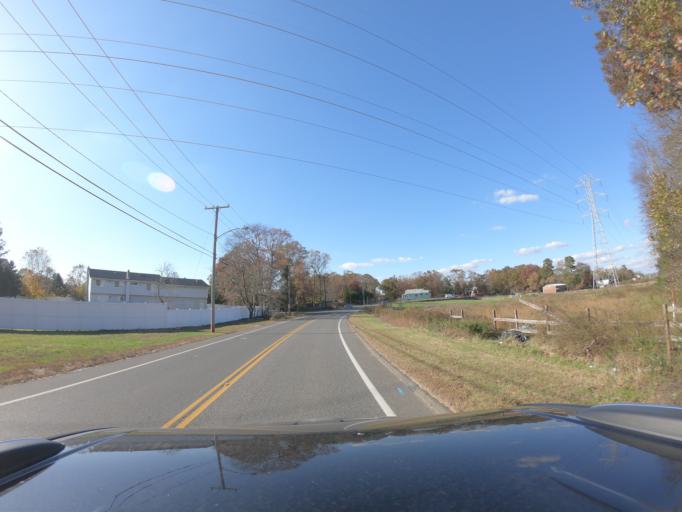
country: US
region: New Jersey
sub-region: Monmouth County
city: Ramtown
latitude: 40.0923
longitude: -74.1557
